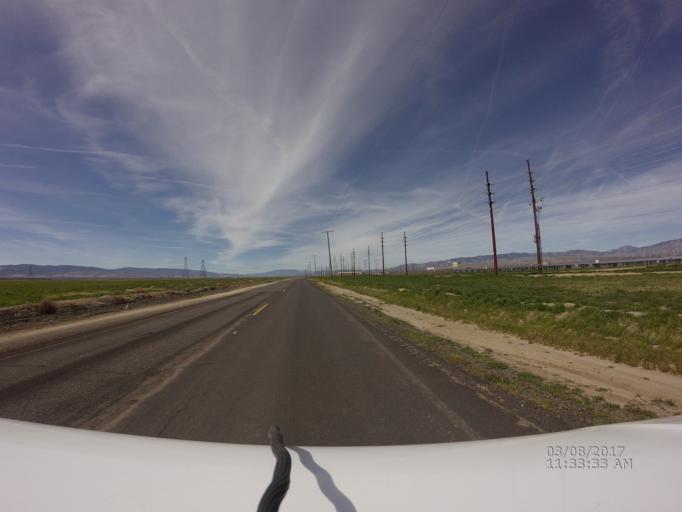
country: US
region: California
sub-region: Los Angeles County
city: Green Valley
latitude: 34.8190
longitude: -118.4021
